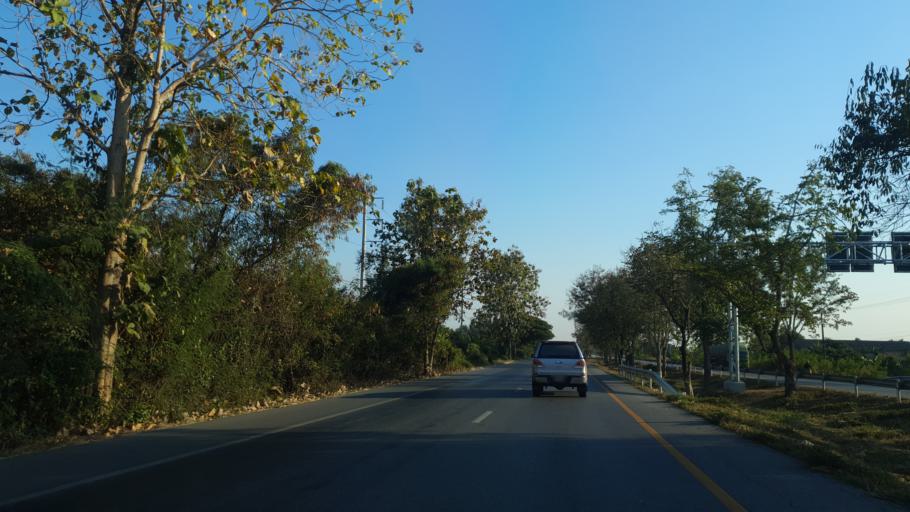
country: TH
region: Kamphaeng Phet
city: Khlong Khlung
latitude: 16.2335
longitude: 99.6961
